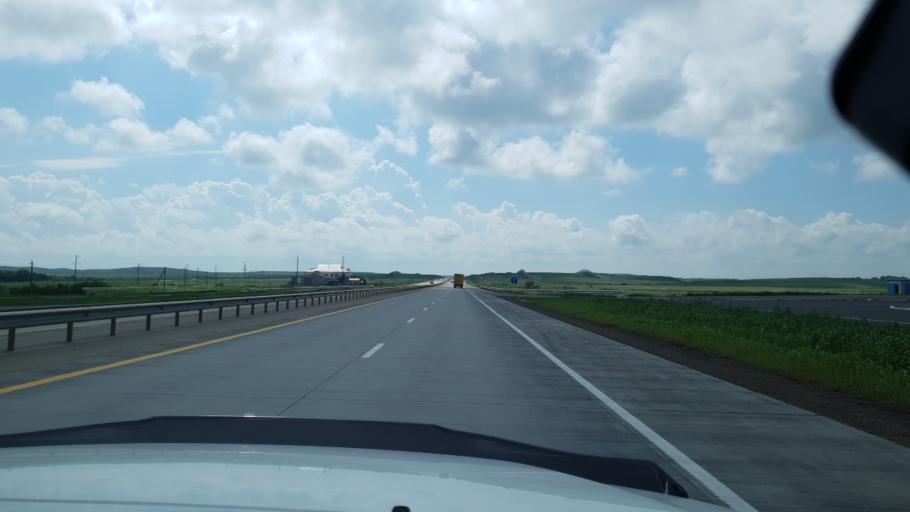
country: KZ
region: Qaraghandy
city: Osakarovka
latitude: 50.7943
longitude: 72.2157
